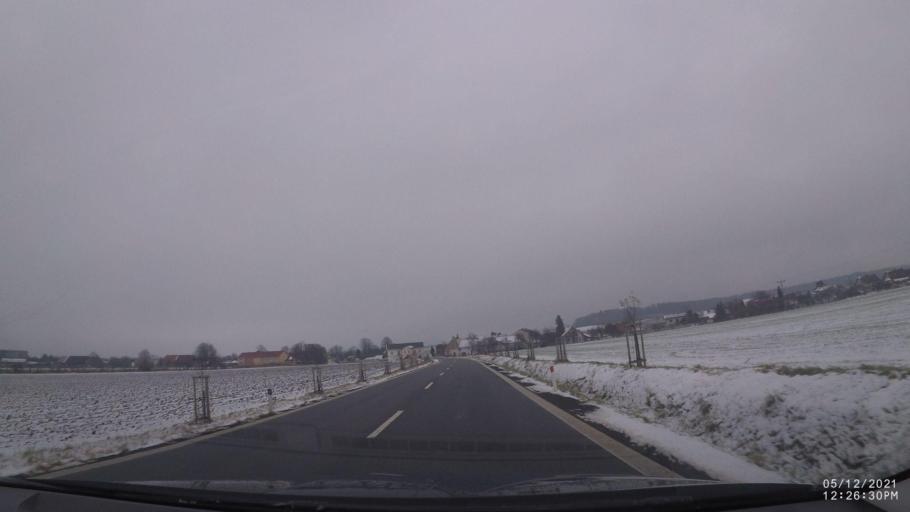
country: CZ
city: Nove Mesto nad Metuji
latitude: 50.3310
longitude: 16.1031
